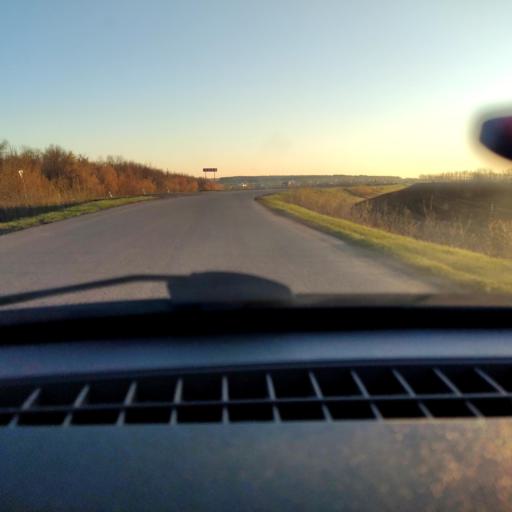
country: RU
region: Bashkortostan
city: Avdon
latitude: 54.5417
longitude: 55.6469
